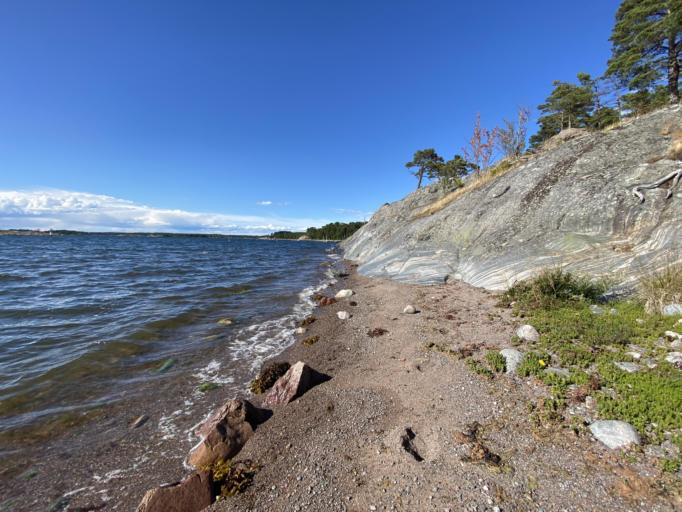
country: SE
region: Stockholm
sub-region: Varmdo Kommun
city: Holo
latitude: 59.2836
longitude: 18.9006
